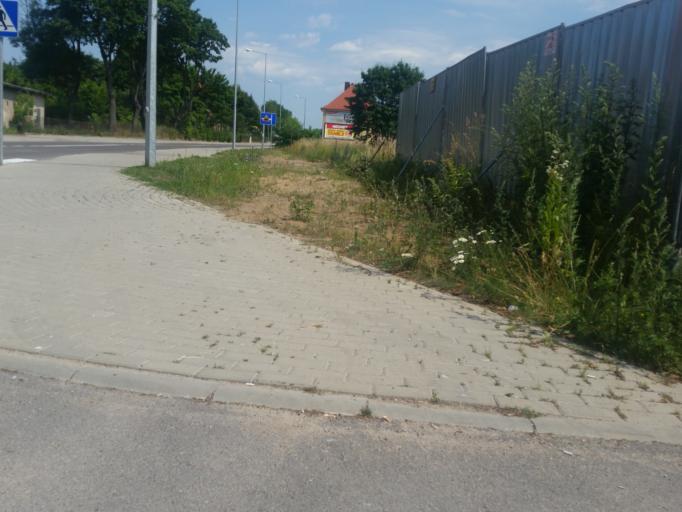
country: PL
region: Warmian-Masurian Voivodeship
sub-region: Powiat goldapski
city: Goldap
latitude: 54.3139
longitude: 22.3102
